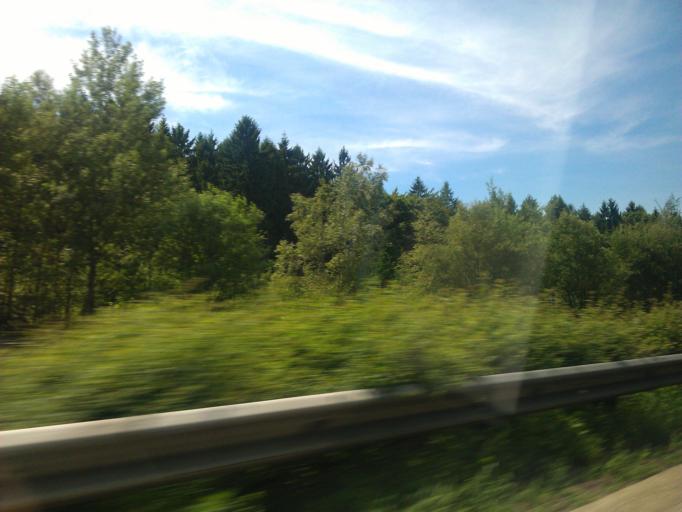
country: DE
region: Rheinland-Pfalz
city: Dernbach
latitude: 50.5368
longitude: 7.5952
